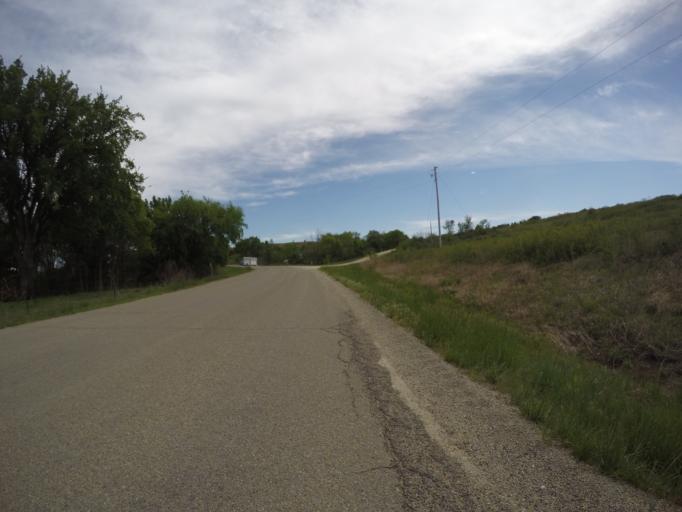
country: US
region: Kansas
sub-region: Riley County
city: Ogden
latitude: 39.0600
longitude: -96.6513
